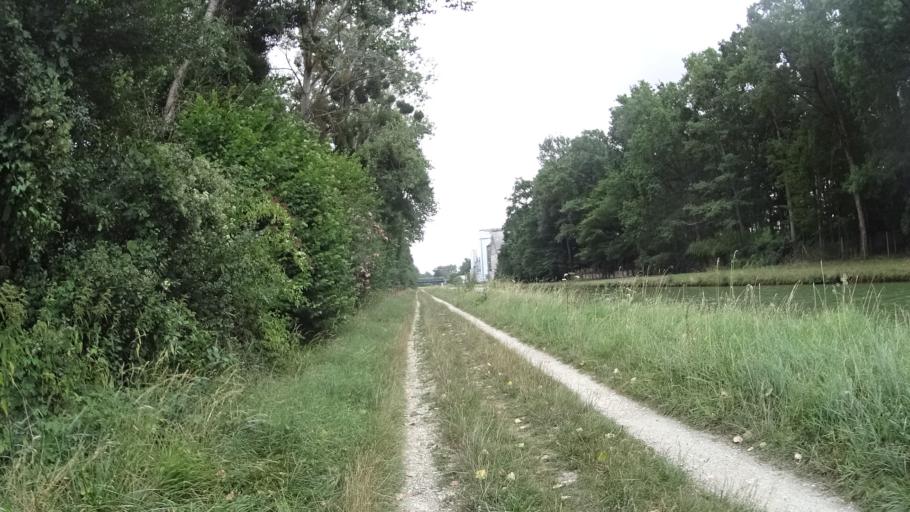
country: FR
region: Centre
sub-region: Departement du Loiret
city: Amilly
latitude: 47.9735
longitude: 2.7522
